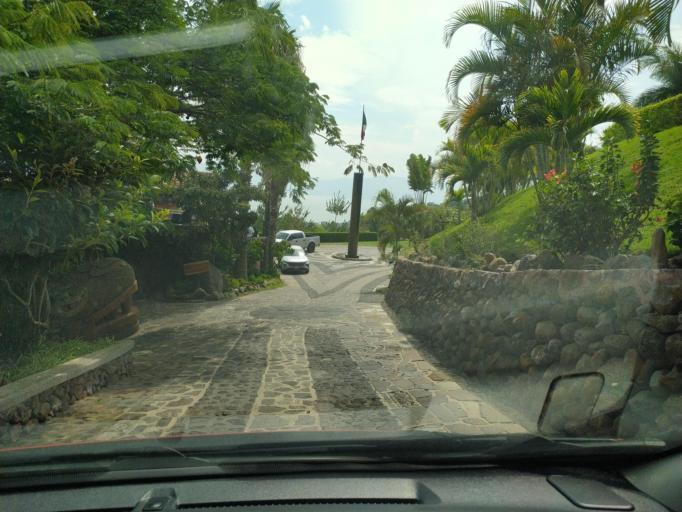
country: MX
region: Jalisco
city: San Juan Cosala
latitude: 20.2896
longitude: -103.3255
